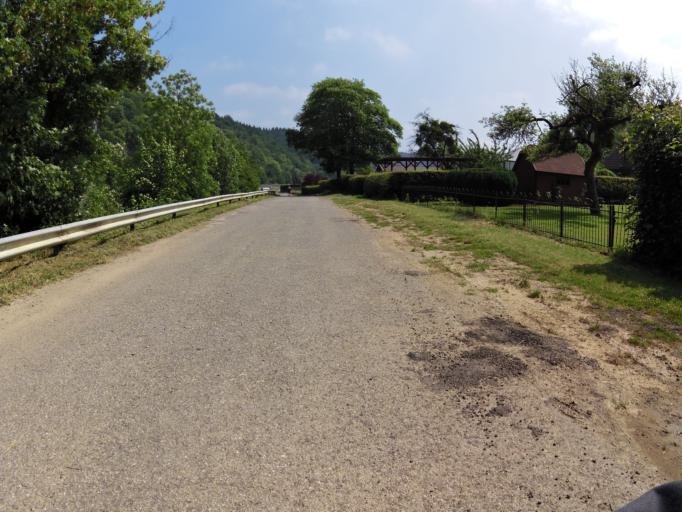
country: BE
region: Wallonia
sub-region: Province de Namur
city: Hastiere-Lavaux
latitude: 50.2127
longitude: 4.8438
